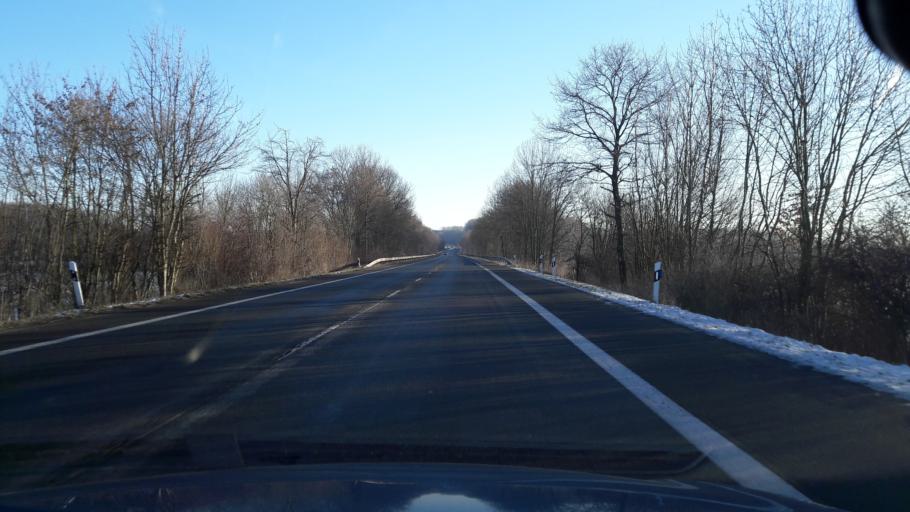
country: DE
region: North Rhine-Westphalia
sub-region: Regierungsbezirk Munster
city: Wadersloh
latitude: 51.7286
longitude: 8.2197
